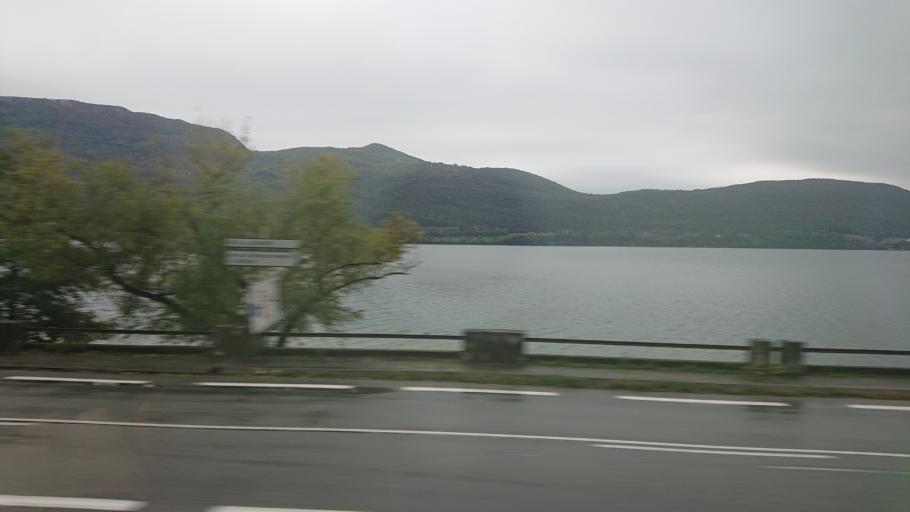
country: FR
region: Rhone-Alpes
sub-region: Departement de la Savoie
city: Brison-Saint-Innocent
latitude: 45.7618
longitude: 5.8705
